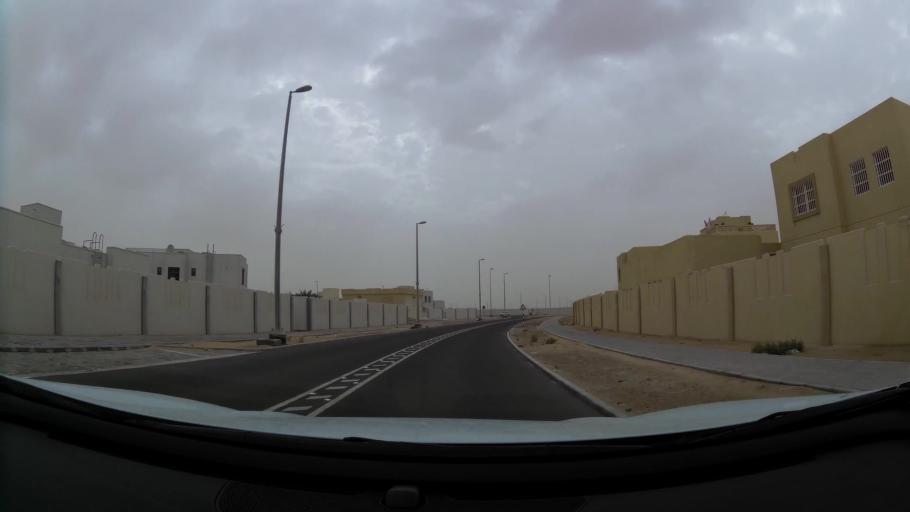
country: AE
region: Abu Dhabi
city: Abu Dhabi
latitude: 24.4429
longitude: 54.7200
